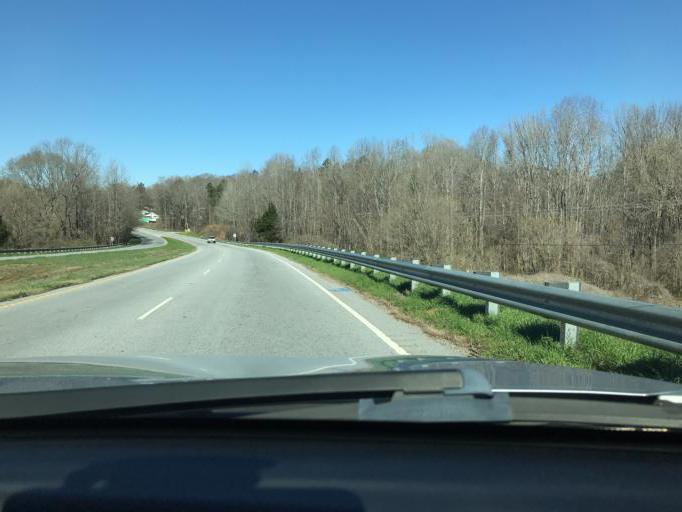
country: US
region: South Carolina
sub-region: Laurens County
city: Watts Mills
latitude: 34.4869
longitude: -81.9583
